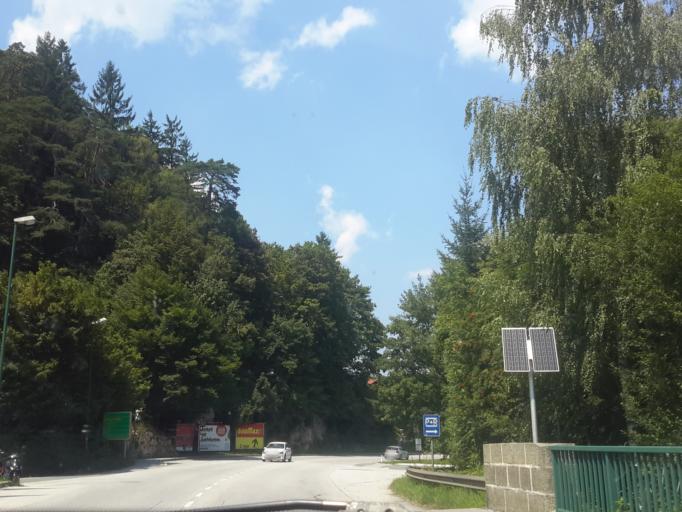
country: AT
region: Tyrol
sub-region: Politischer Bezirk Kufstein
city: Kufstein
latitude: 47.5791
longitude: 12.1622
